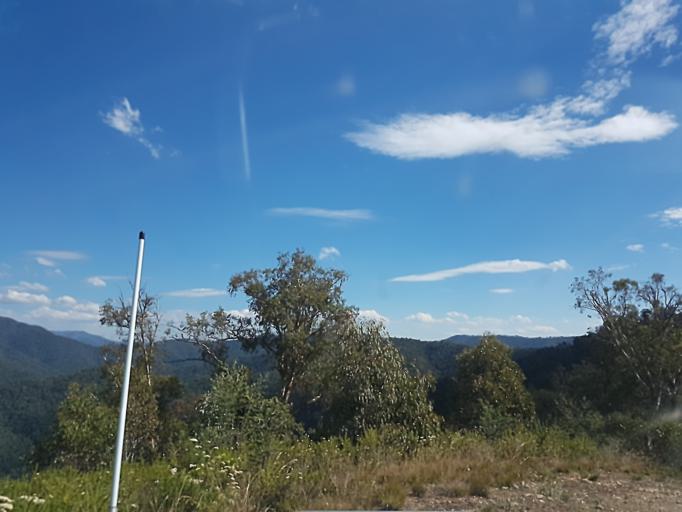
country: AU
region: Victoria
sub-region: Alpine
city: Mount Beauty
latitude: -36.9088
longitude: 147.0215
